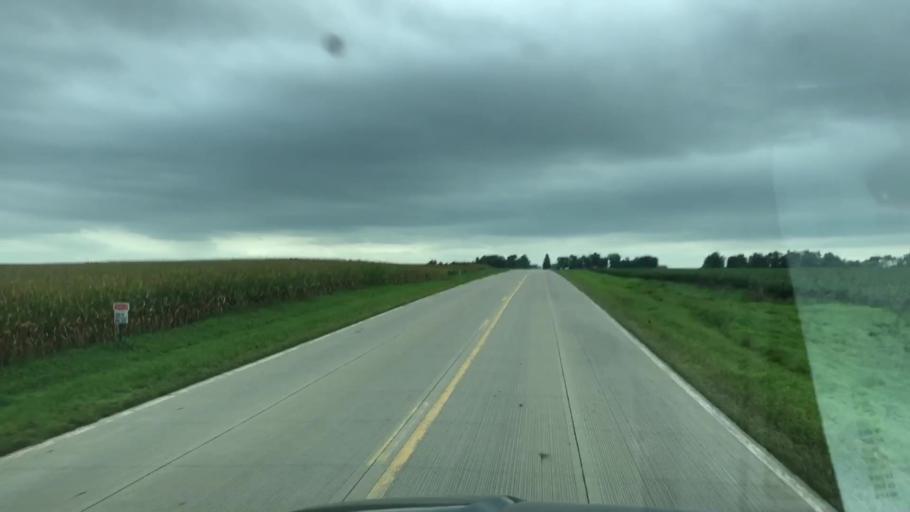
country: US
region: Iowa
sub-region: Sioux County
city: Alton
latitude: 43.1182
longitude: -95.9789
